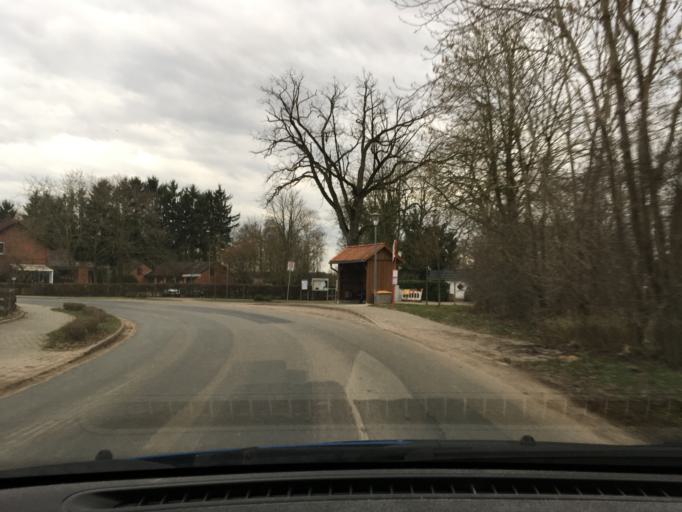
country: DE
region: Lower Saxony
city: Handorf
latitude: 53.3655
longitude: 10.3346
